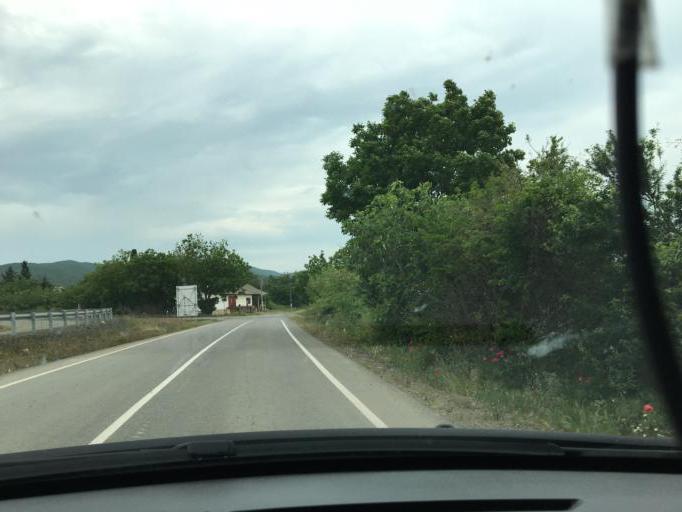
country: MK
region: Gevgelija
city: Miravci
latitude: 41.3048
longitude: 22.4426
